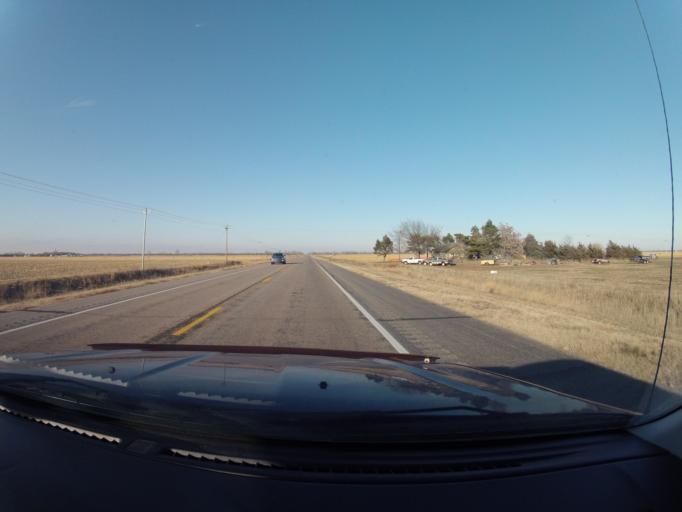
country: US
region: Nebraska
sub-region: Kearney County
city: Minden
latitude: 40.6327
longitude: -98.9514
